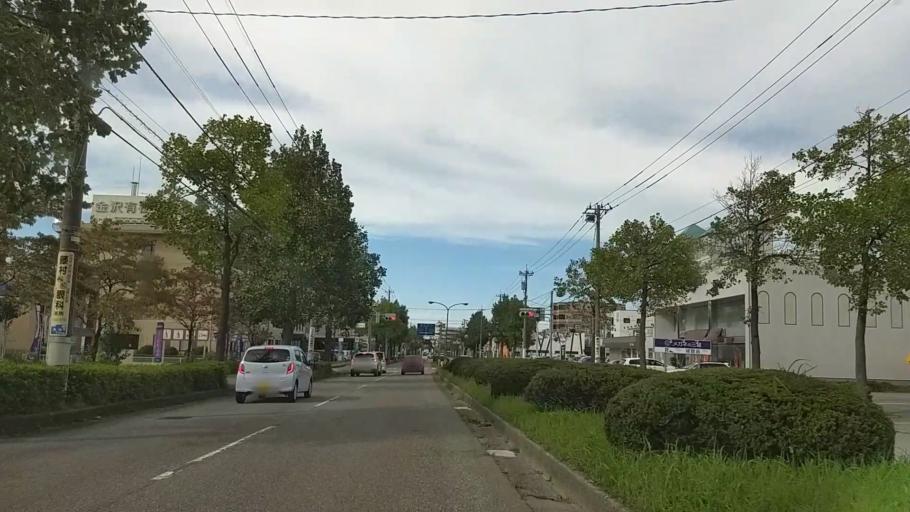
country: JP
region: Ishikawa
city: Nonoichi
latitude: 36.5379
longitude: 136.6394
